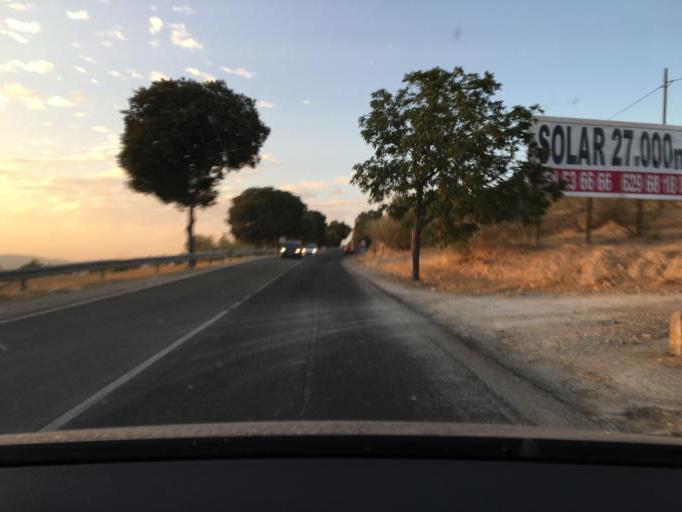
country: ES
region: Andalusia
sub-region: Provincia de Granada
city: Granada
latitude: 37.1916
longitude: -3.5928
